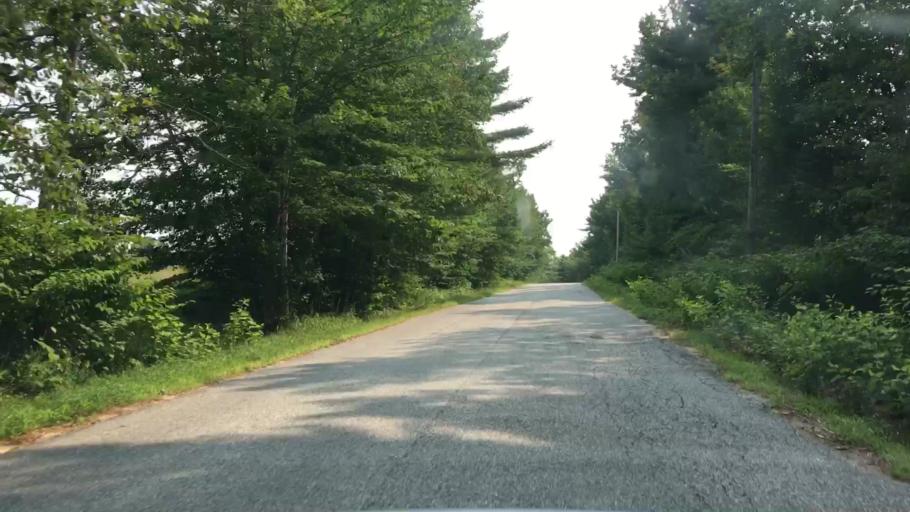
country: US
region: Maine
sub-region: Androscoggin County
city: Livermore
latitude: 44.3253
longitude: -70.2898
